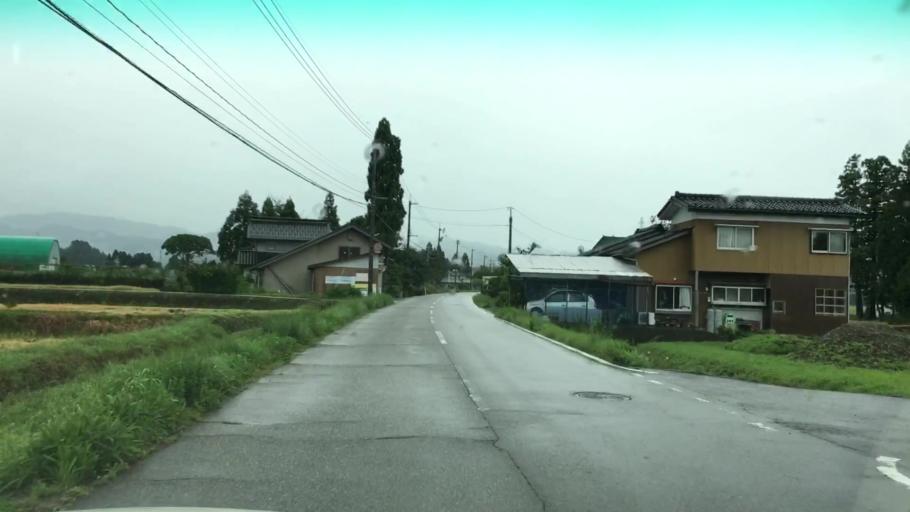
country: JP
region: Toyama
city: Kamiichi
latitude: 36.6208
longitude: 137.3232
